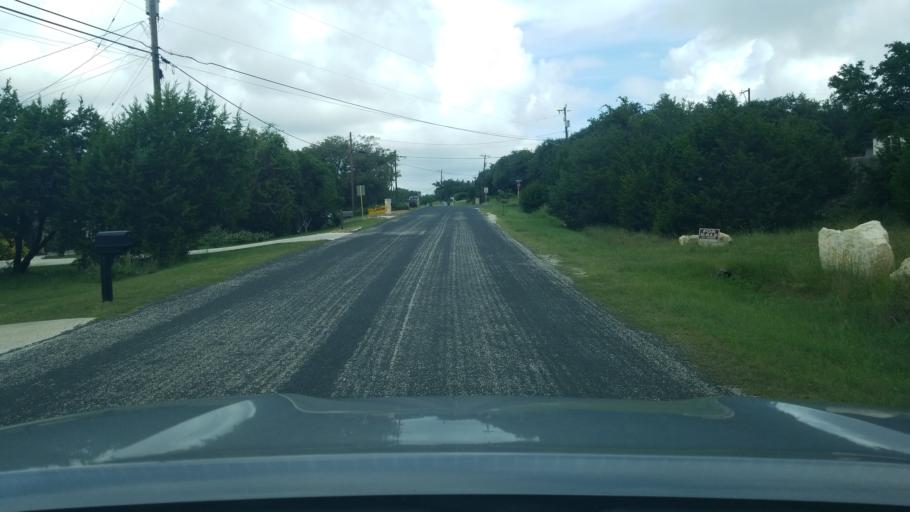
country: US
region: Texas
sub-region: Bexar County
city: Timberwood Park
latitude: 29.6878
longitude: -98.5000
